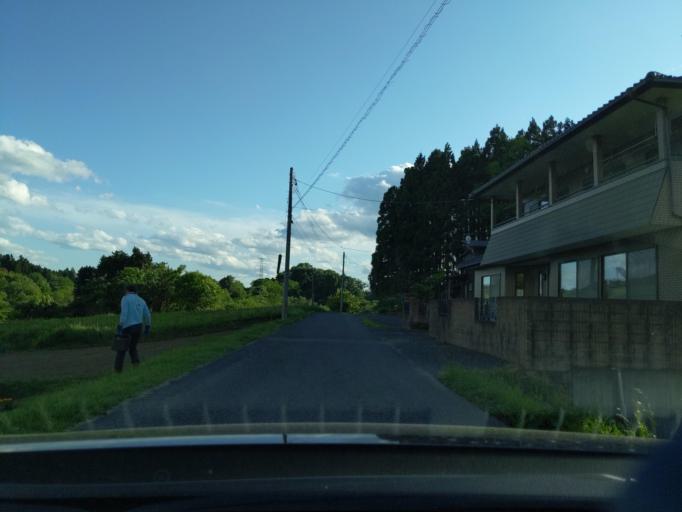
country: JP
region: Fukushima
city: Miharu
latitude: 37.4209
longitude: 140.4560
